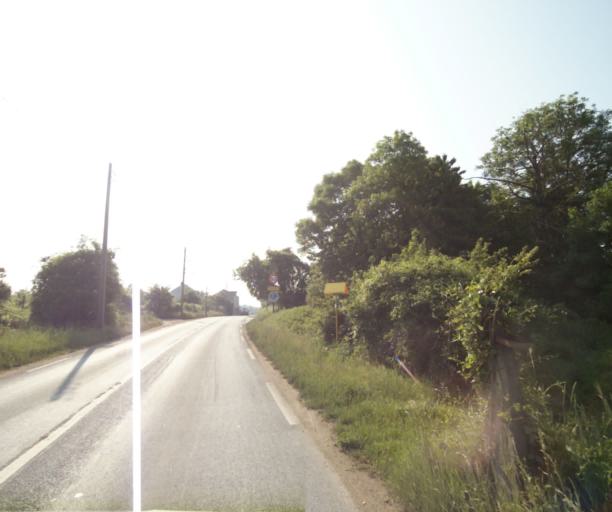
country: FR
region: Ile-de-France
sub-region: Departement du Val-d'Oise
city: Cormeilles-en-Parisis
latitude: 48.9619
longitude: 2.2207
